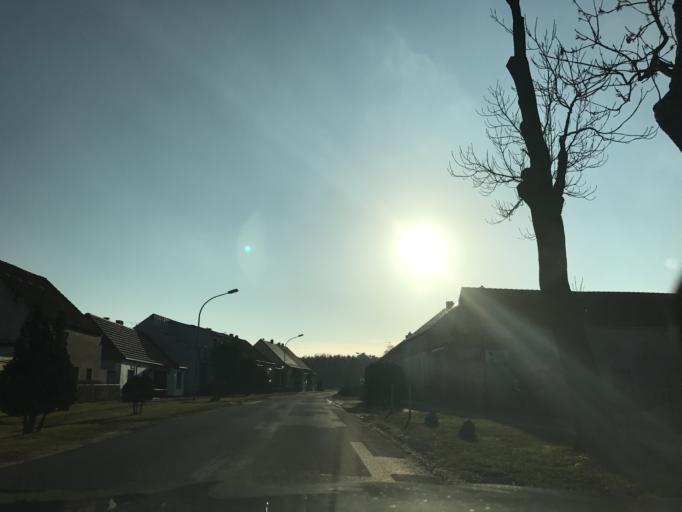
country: DE
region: Brandenburg
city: Wenzlow
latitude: 52.2967
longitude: 12.4542
